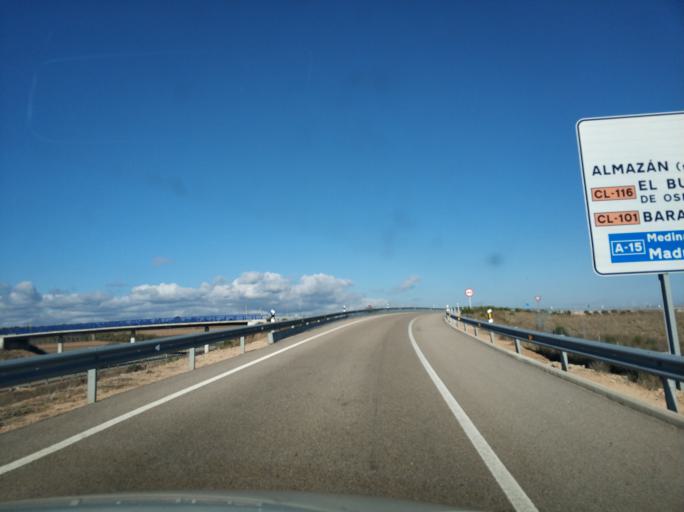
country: ES
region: Castille and Leon
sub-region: Provincia de Soria
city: Almazan
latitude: 41.4696
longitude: -2.5239
